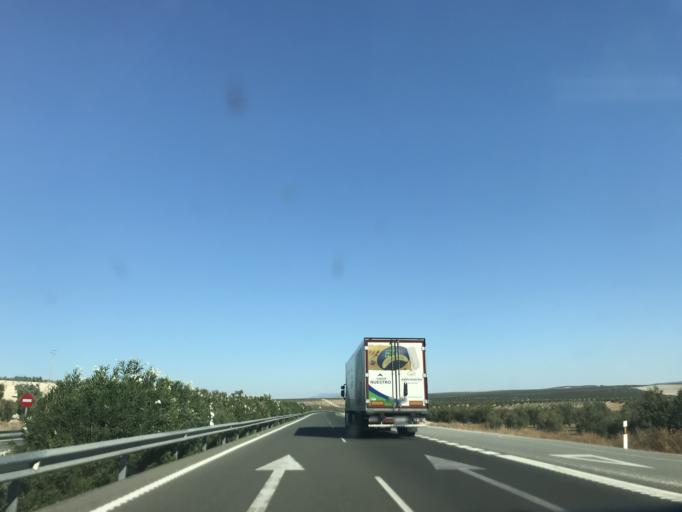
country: ES
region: Andalusia
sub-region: Provincia de Sevilla
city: La Puebla de Cazalla
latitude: 37.2305
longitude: -5.2553
